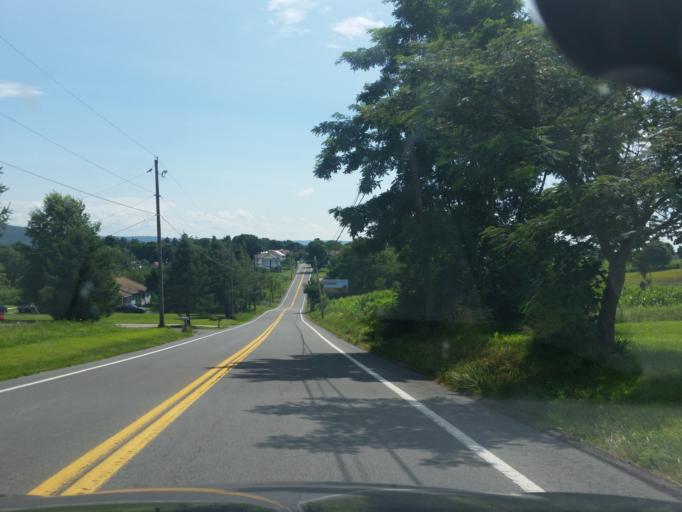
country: US
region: Pennsylvania
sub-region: Dauphin County
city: Matamoras
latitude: 40.5042
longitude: -76.8819
